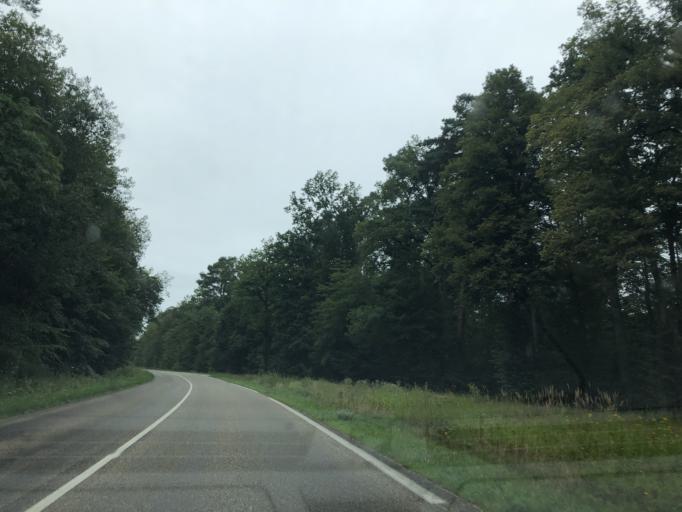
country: DE
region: Rheinland-Pfalz
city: Steinfeld
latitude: 48.9945
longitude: 8.0750
